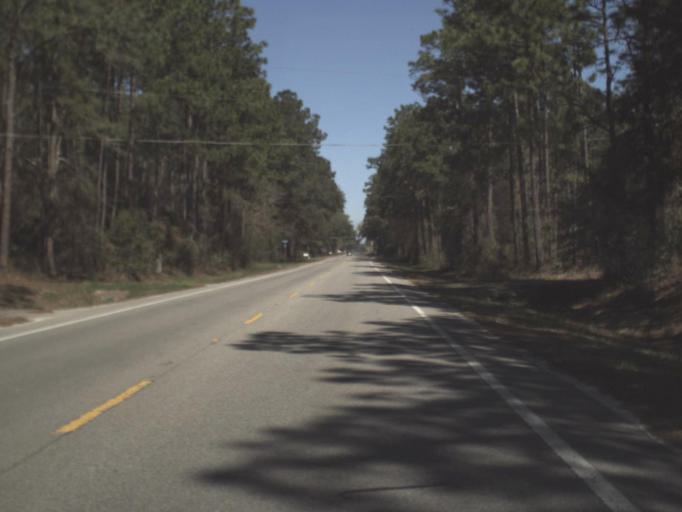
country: US
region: Florida
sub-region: Leon County
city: Woodville
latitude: 30.3166
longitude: -84.3116
